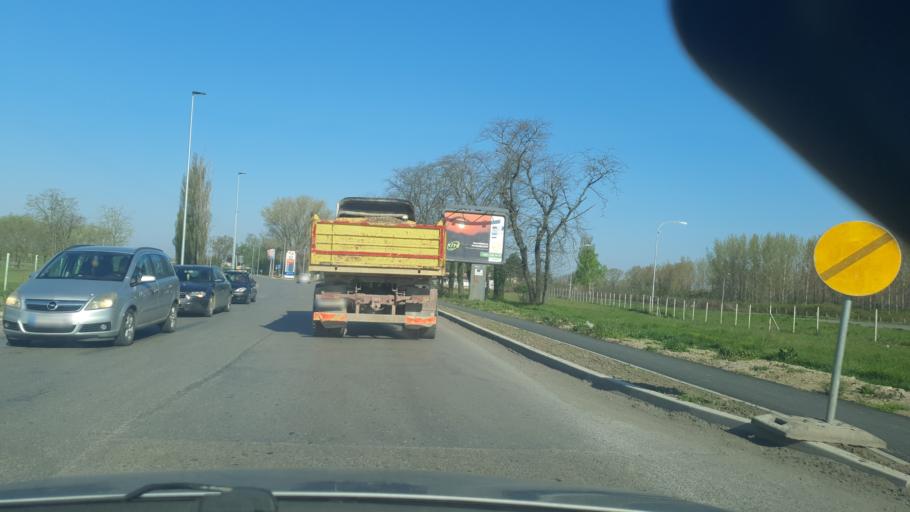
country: RS
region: Autonomna Pokrajina Vojvodina
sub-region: Juznobacki Okrug
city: Vrbas
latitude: 45.5819
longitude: 19.6196
